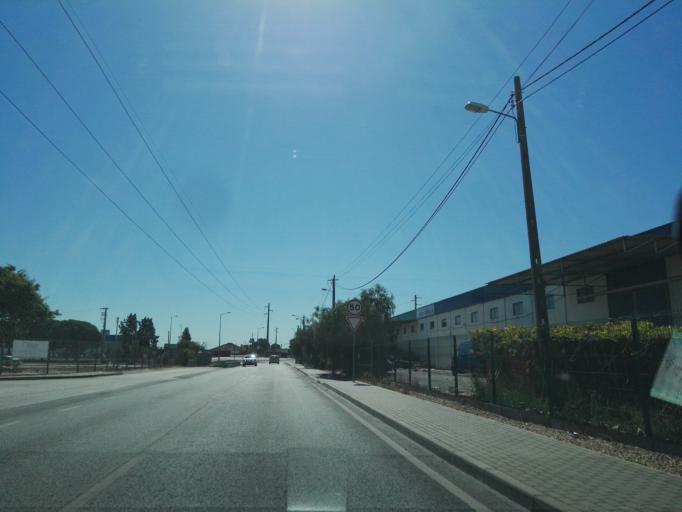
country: PT
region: Santarem
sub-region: Benavente
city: Samora Correia
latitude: 38.9141
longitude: -8.8543
